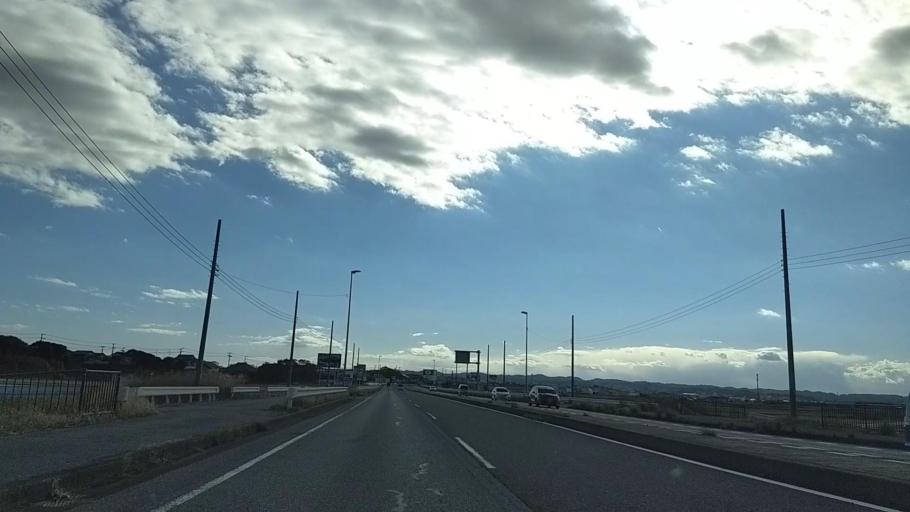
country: JP
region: Chiba
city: Tateyama
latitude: 35.0226
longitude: 139.8678
